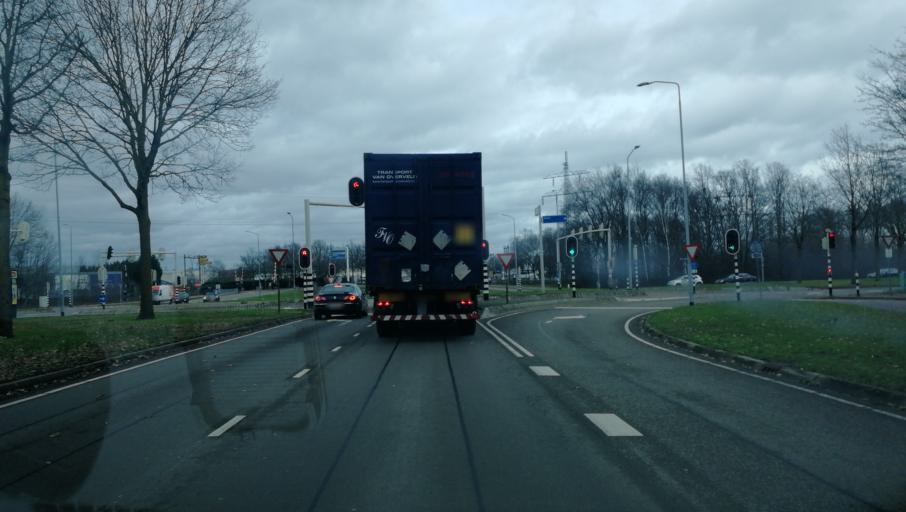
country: NL
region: Limburg
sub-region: Gemeente Venlo
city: Venlo
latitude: 51.3790
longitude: 6.1371
